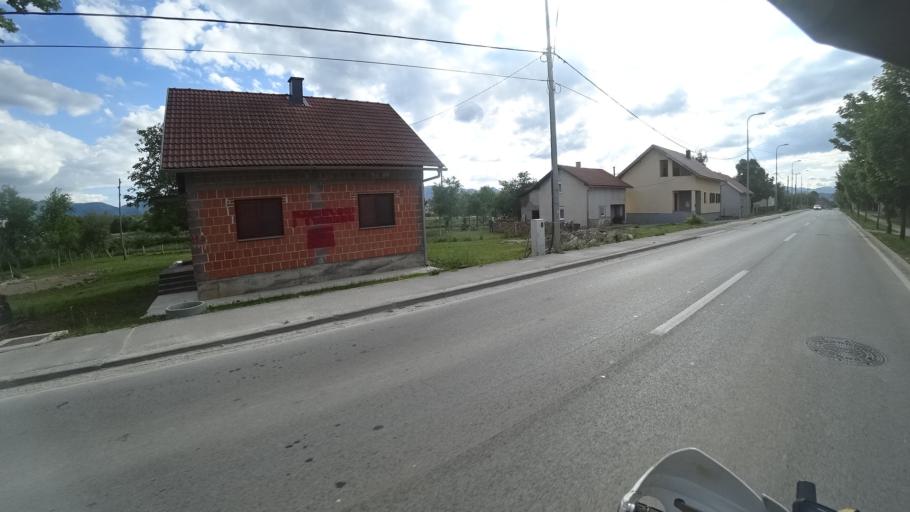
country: HR
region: Licko-Senjska
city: Gospic
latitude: 44.5362
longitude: 15.3919
